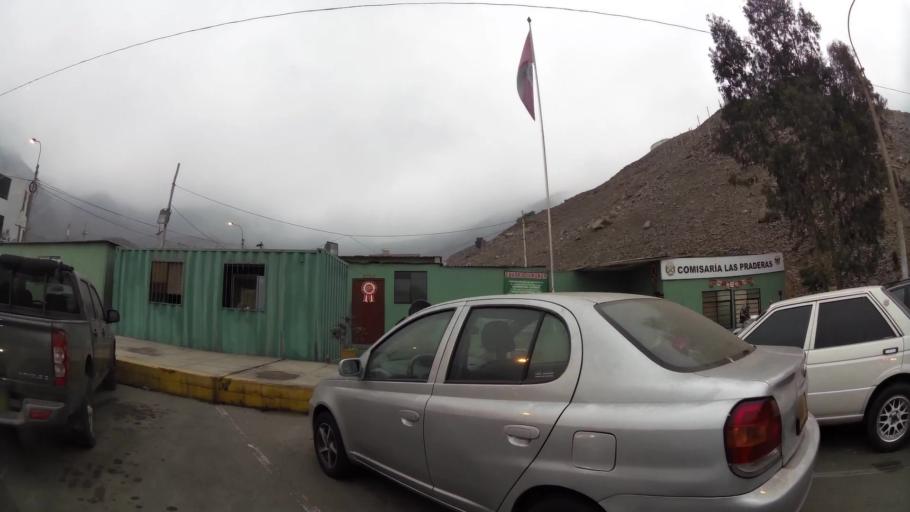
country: PE
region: Lima
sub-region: Lima
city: La Molina
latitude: -12.1146
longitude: -76.9371
